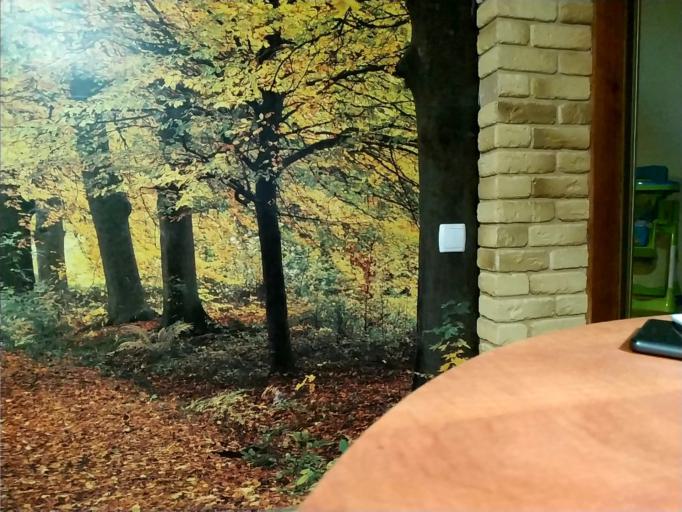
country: BY
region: Minsk
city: Plyeshchanitsy
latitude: 54.4288
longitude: 27.6444
